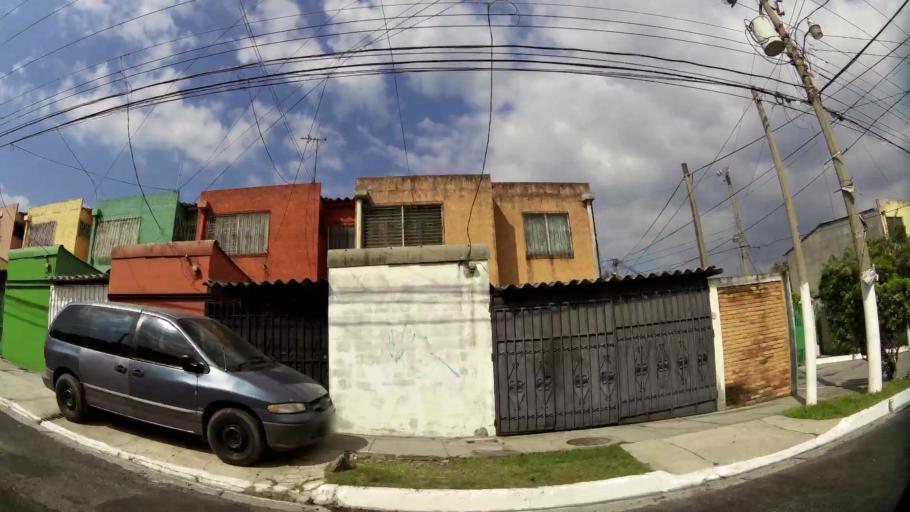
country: SV
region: San Salvador
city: Mejicanos
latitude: 13.7331
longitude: -89.2094
